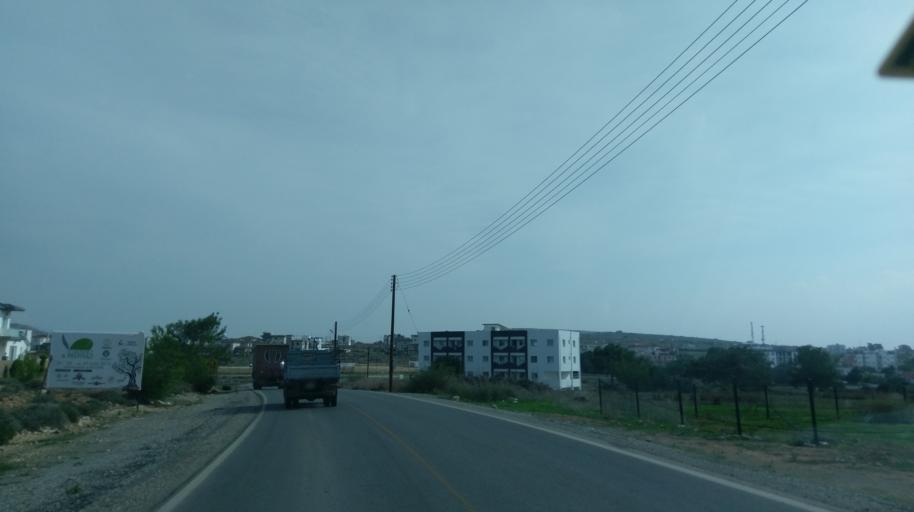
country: CY
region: Lefkosia
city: Morfou
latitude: 35.2508
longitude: 33.0347
